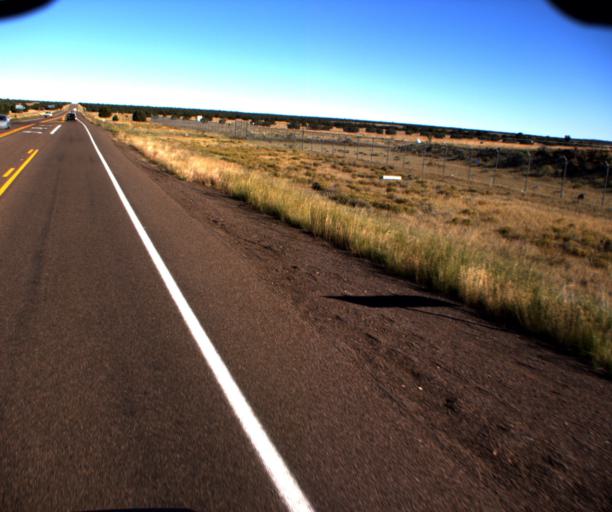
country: US
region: Arizona
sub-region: Navajo County
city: Show Low
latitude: 34.2634
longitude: -110.0204
